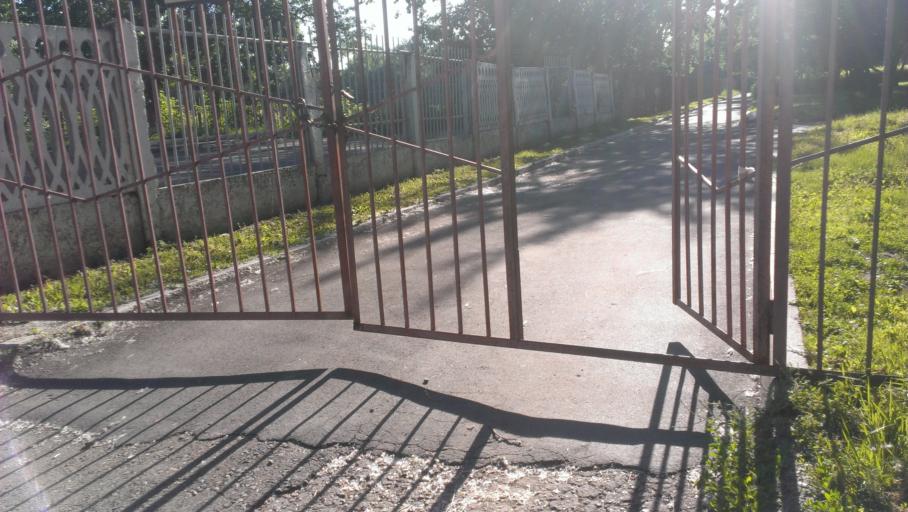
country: RU
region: Altai Krai
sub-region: Gorod Barnaulskiy
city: Barnaul
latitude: 53.3670
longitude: 83.7009
